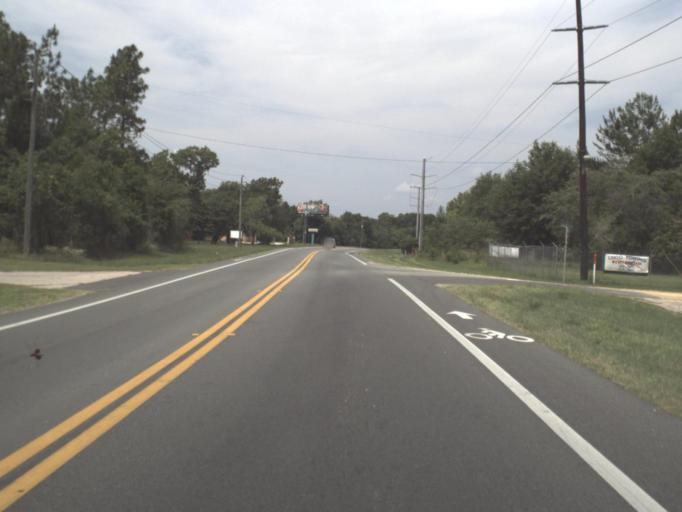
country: US
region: Florida
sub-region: Putnam County
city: Interlachen
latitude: 29.6252
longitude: -81.9064
